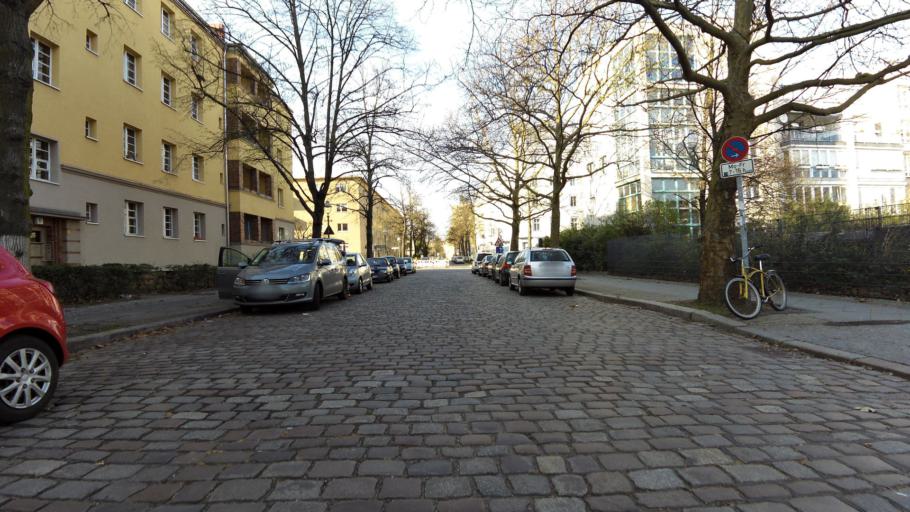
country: DE
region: Berlin
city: Wilmersdorf Bezirk
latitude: 52.4847
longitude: 13.3157
